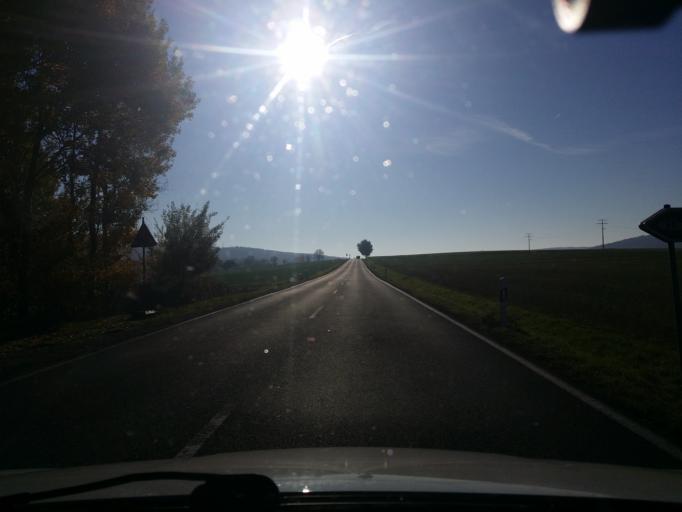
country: DE
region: Hesse
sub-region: Regierungsbezirk Darmstadt
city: Idstein
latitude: 50.1969
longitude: 8.2835
